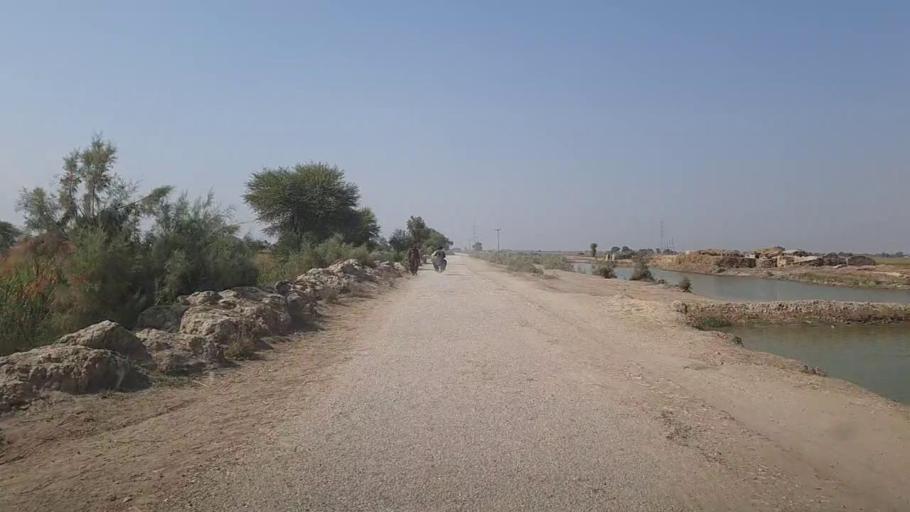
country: PK
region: Sindh
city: Kandhkot
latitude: 28.4057
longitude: 69.2541
